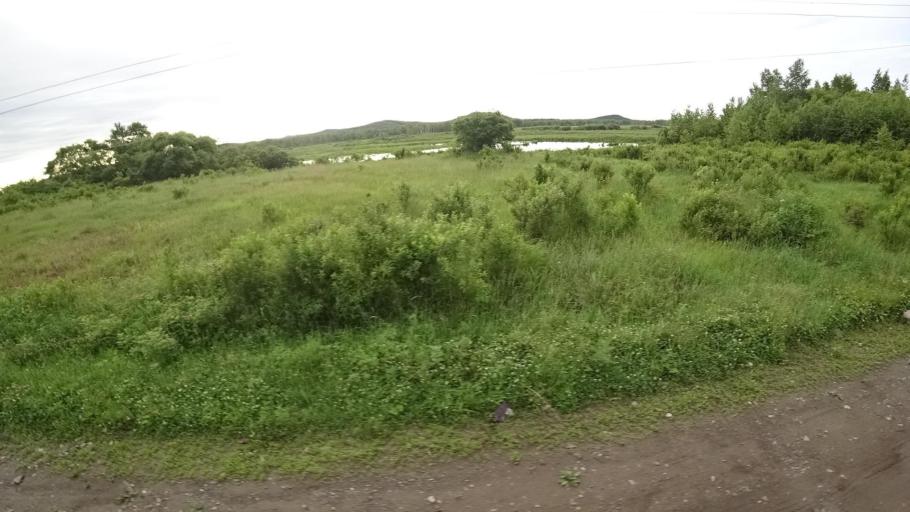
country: RU
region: Khabarovsk Krai
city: Amursk
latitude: 49.8870
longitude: 136.1283
